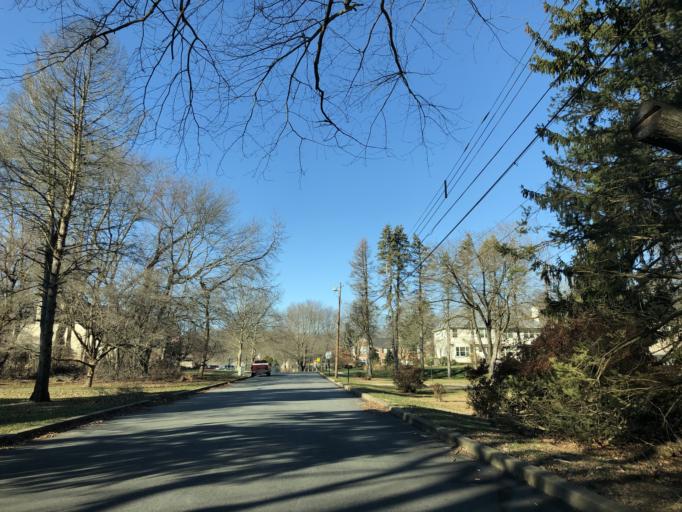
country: US
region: Pennsylvania
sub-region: Delaware County
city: Chester Heights
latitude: 39.8566
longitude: -75.4679
